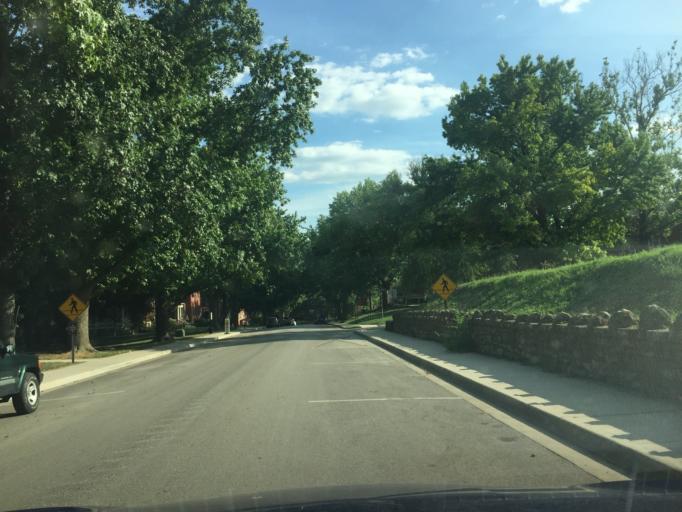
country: US
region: Kansas
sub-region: Leavenworth County
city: Leavenworth
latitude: 39.3548
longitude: -94.9199
